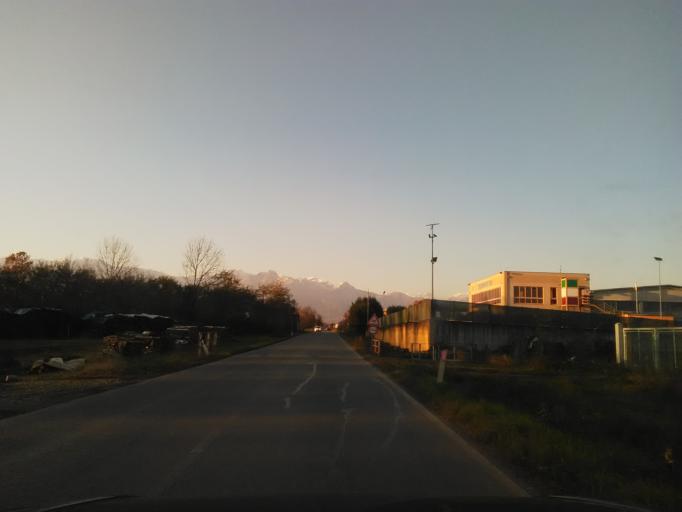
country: IT
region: Piedmont
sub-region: Provincia di Biella
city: Cerrione
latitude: 45.4812
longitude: 8.0732
